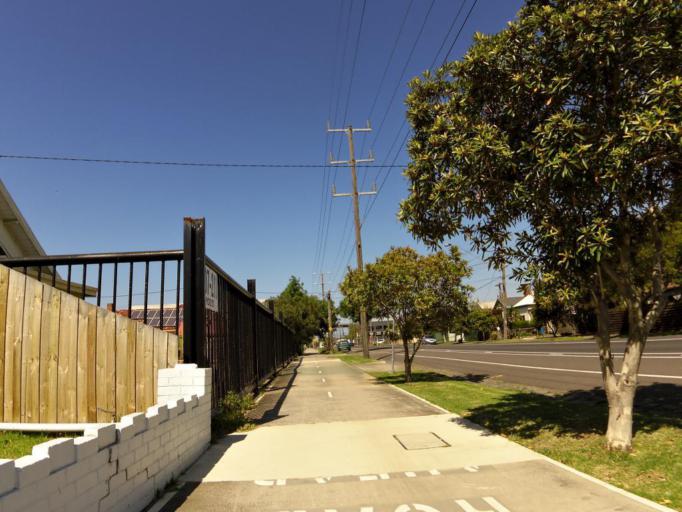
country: AU
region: Victoria
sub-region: Maribyrnong
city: Yarraville
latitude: -37.8186
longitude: 144.8965
